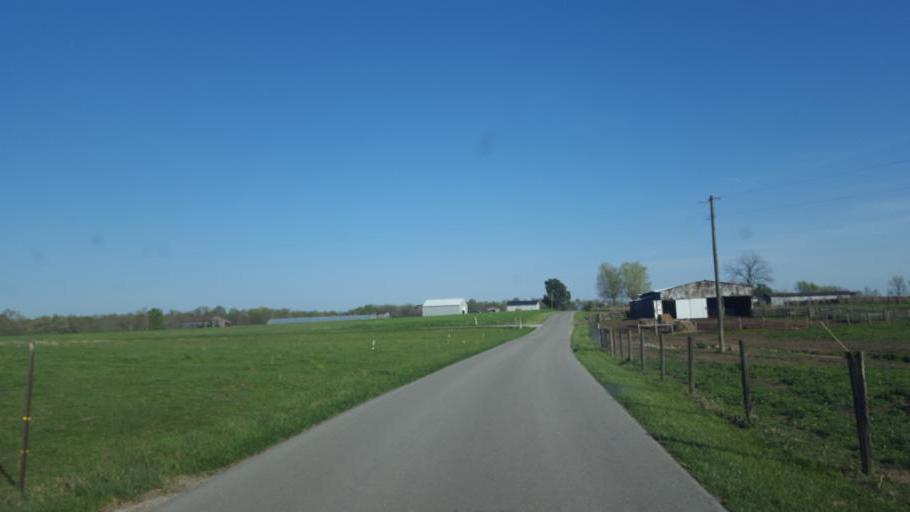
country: US
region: Kentucky
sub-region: Barren County
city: Cave City
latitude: 37.1675
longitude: -85.9832
